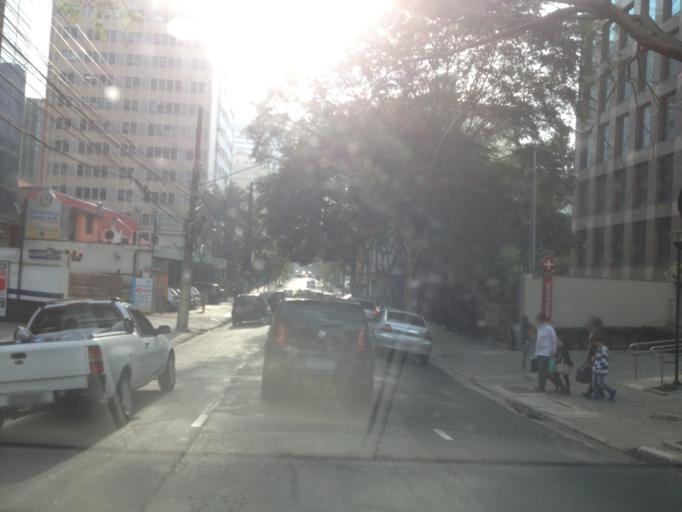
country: BR
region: Sao Paulo
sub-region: Sao Paulo
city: Sao Paulo
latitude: -23.5685
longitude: -46.6459
